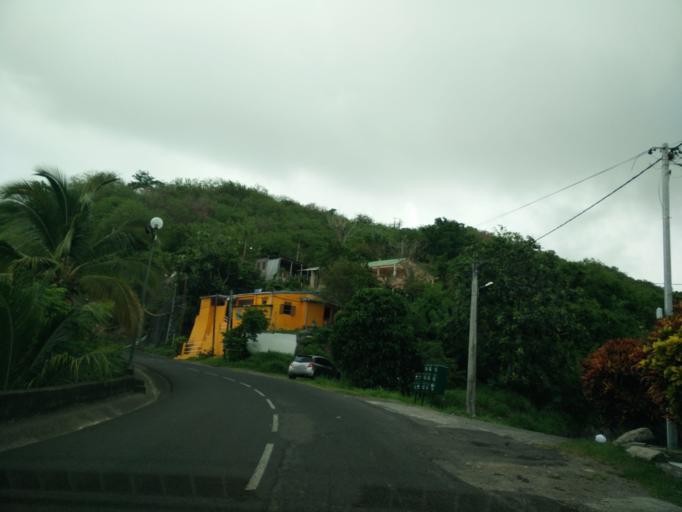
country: MQ
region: Martinique
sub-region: Martinique
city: Saint-Pierre
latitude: 14.8069
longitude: -61.2258
